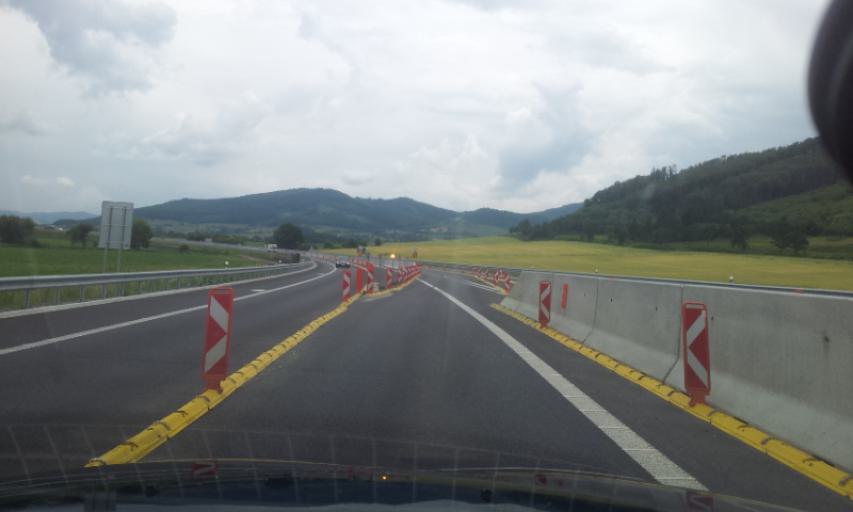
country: SK
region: Banskobystricky
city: Detva
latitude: 48.5428
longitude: 19.3324
